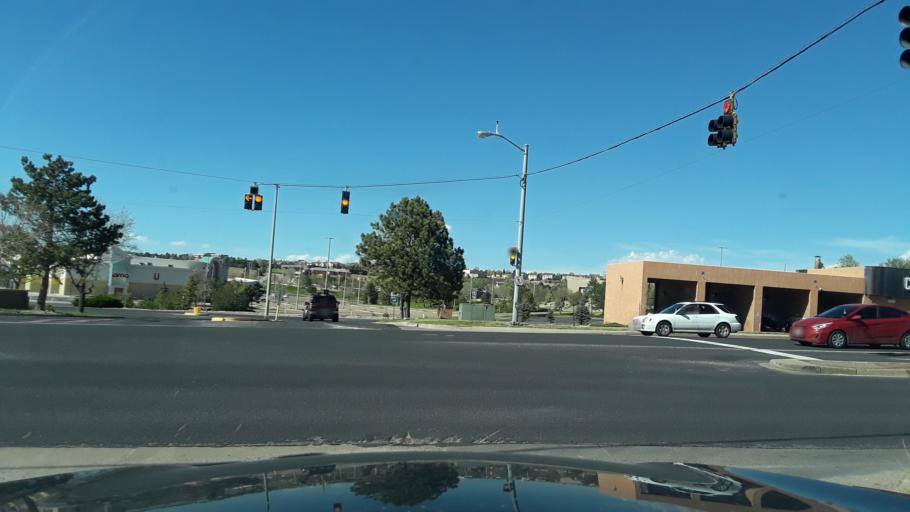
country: US
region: Colorado
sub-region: El Paso County
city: Air Force Academy
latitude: 38.9448
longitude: -104.7939
